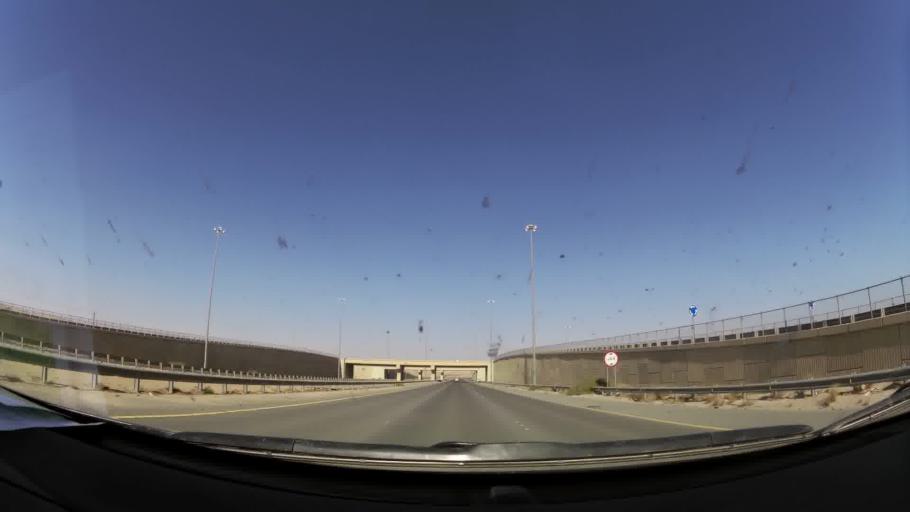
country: KW
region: Muhafazat al Jahra'
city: Al Jahra'
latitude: 29.4721
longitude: 47.7674
